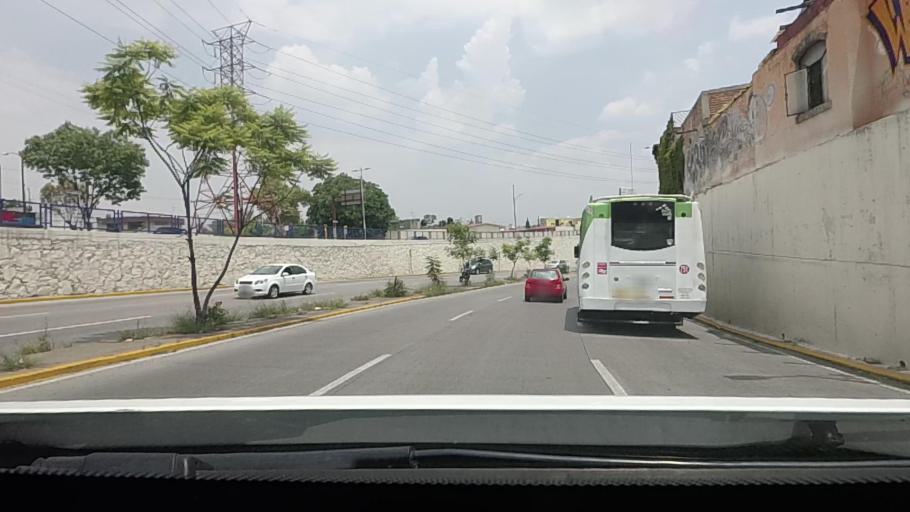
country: MX
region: Mexico
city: Naucalpan de Juarez
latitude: 19.4978
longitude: -99.2502
